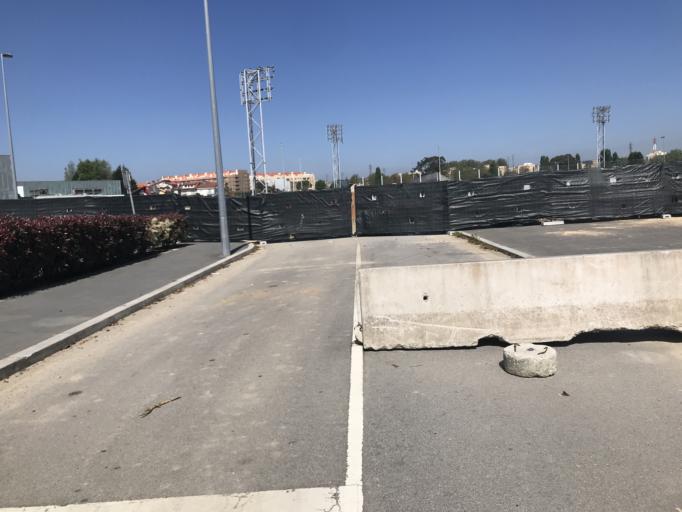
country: PT
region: Porto
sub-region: Matosinhos
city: Senhora da Hora
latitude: 41.1833
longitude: -8.6683
